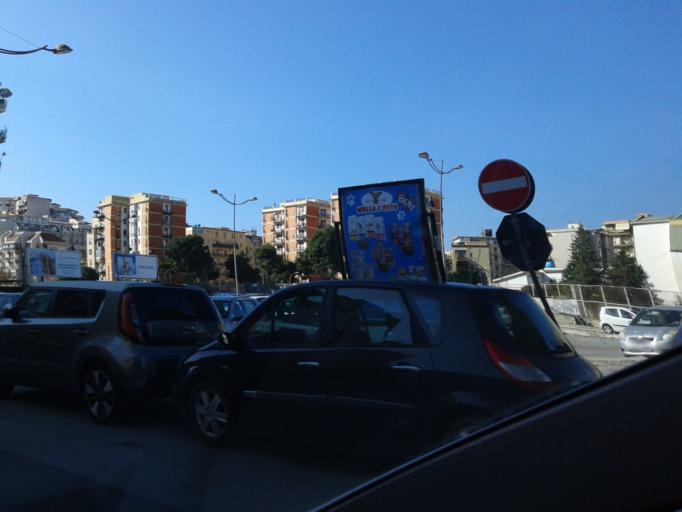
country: IT
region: Sicily
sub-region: Palermo
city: Palermo
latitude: 38.1315
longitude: 13.3427
